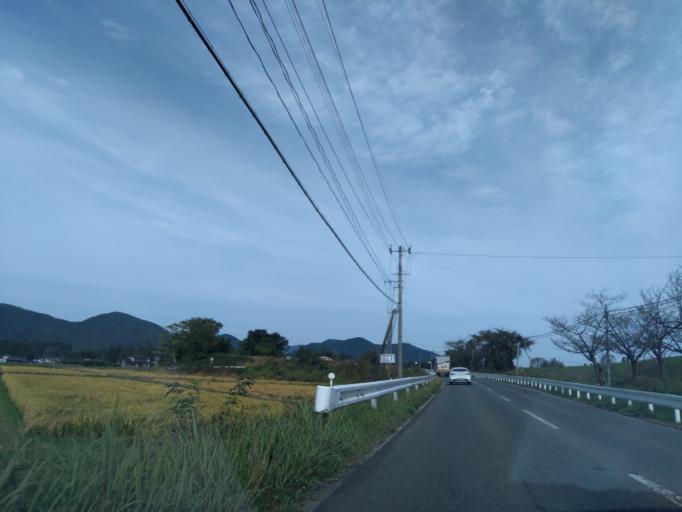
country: JP
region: Iwate
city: Hanamaki
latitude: 39.4296
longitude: 141.0840
